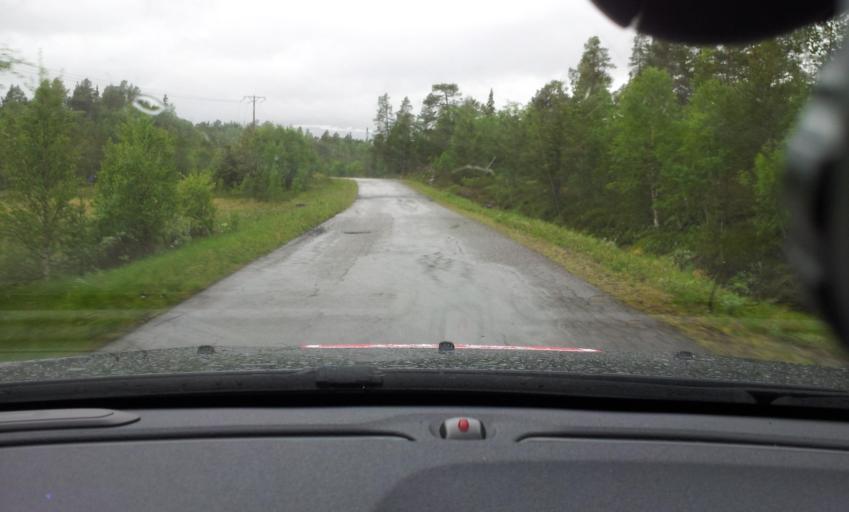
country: SE
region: Jaemtland
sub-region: Are Kommun
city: Are
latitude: 63.1491
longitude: 12.9388
